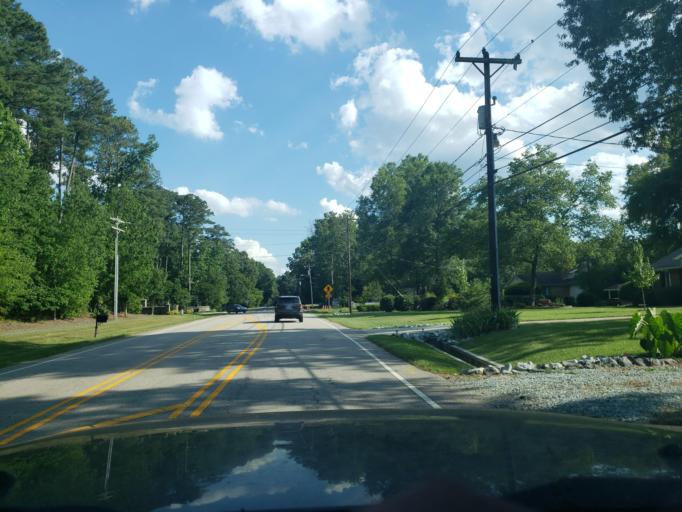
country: US
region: North Carolina
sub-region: Durham County
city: Durham
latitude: 35.9795
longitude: -78.9900
